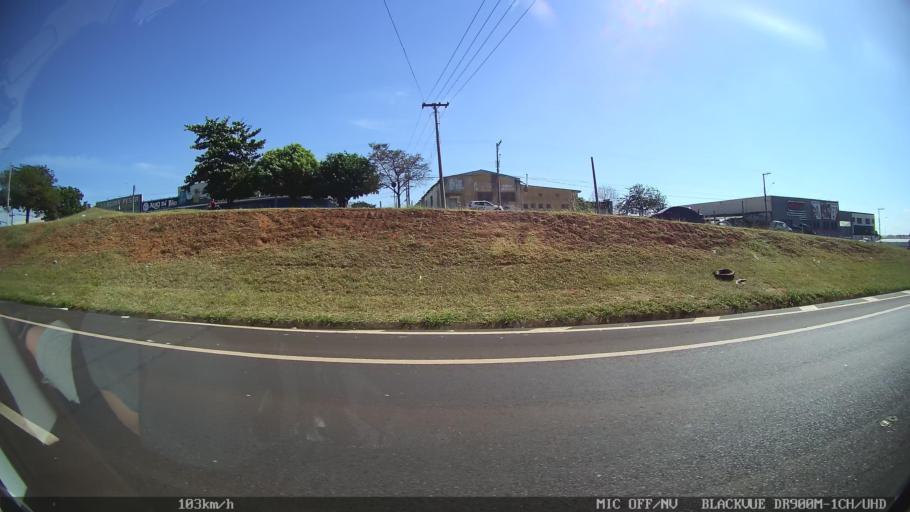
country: BR
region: Sao Paulo
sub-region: Franca
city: Franca
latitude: -20.5283
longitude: -47.4223
